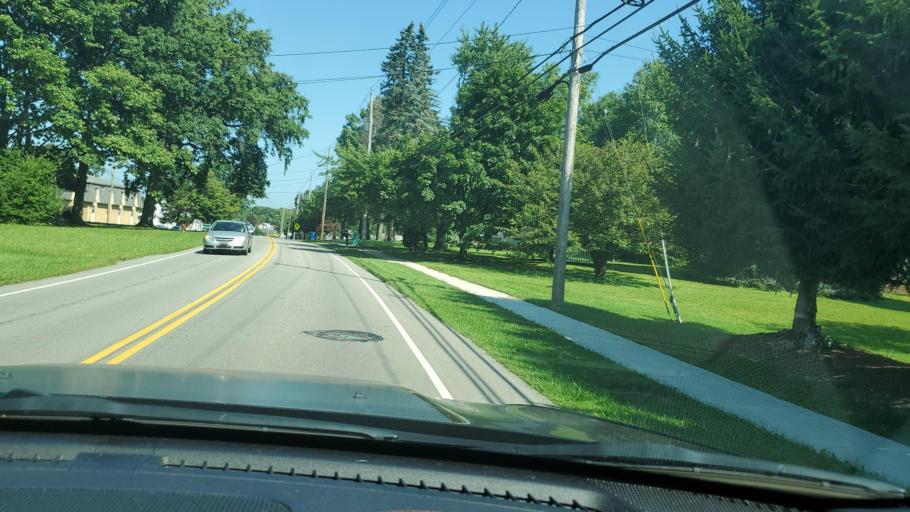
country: US
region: Ohio
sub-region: Trumbull County
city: Girard
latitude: 41.1683
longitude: -80.6895
